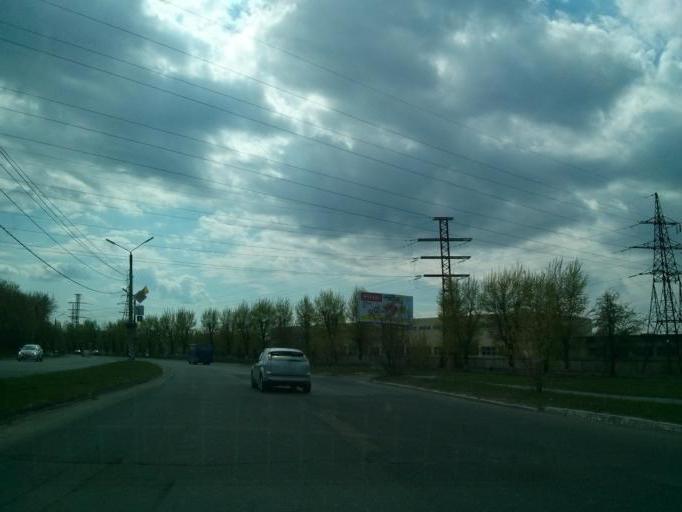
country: RU
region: Vladimir
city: Murom
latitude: 55.5608
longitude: 42.0591
